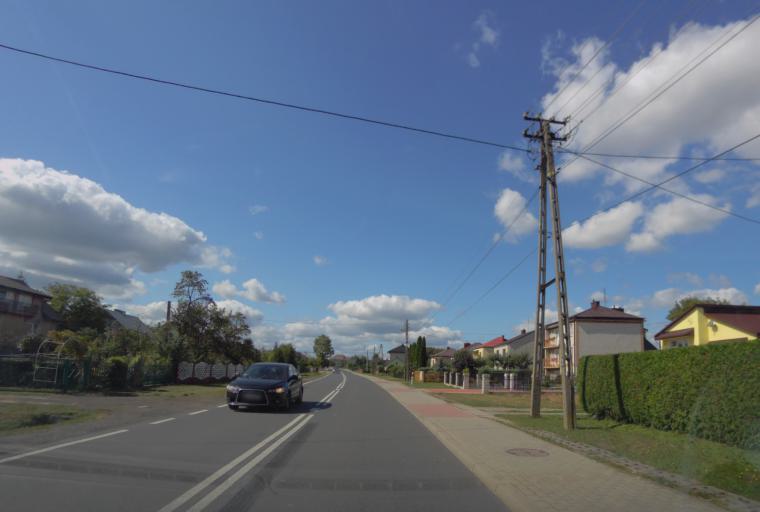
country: PL
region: Subcarpathian Voivodeship
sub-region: Powiat nizanski
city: Jezowe
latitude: 50.3756
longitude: 22.1342
